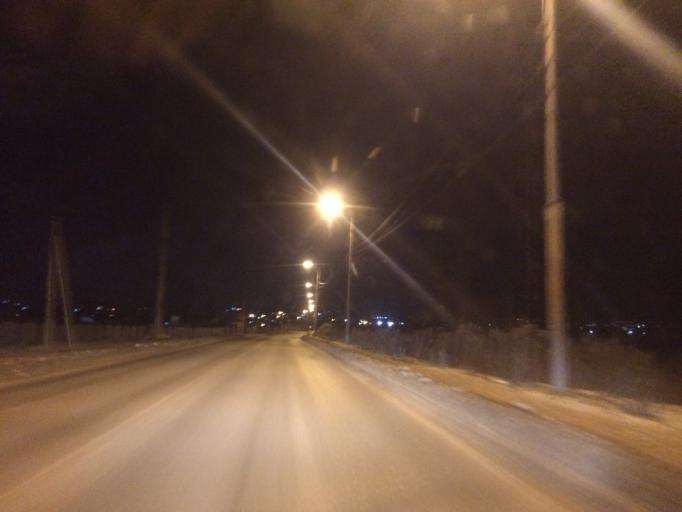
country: RU
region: Tula
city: Mendeleyevskiy
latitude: 54.1480
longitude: 37.6012
